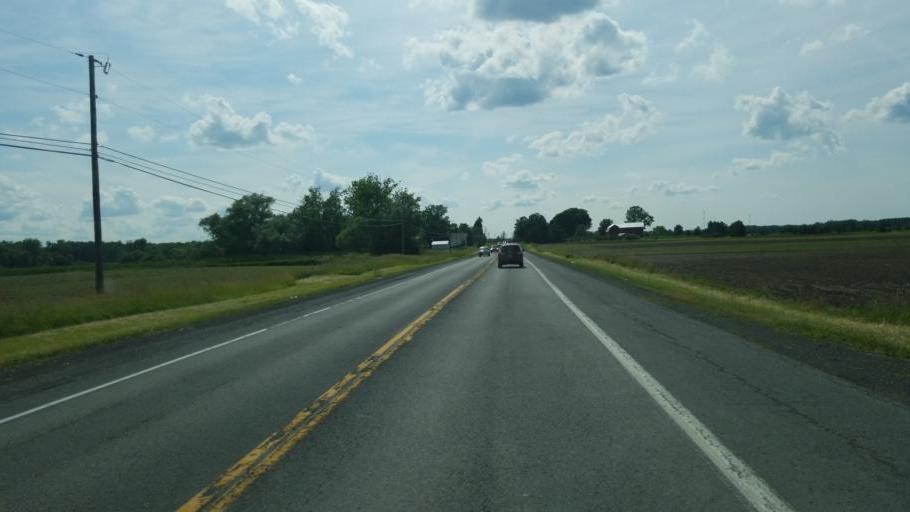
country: US
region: New York
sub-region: Ontario County
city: Clifton Springs
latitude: 42.8607
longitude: -77.1607
